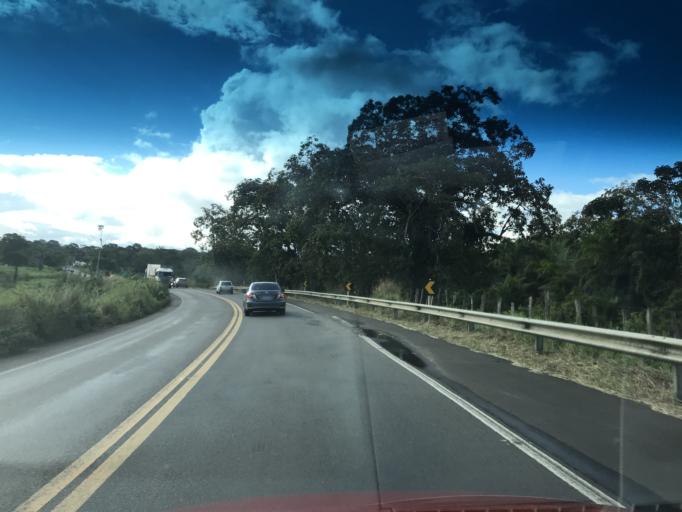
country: BR
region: Bahia
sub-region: Ibirapitanga
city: Ibirapitanga
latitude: -14.1555
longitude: -39.3266
